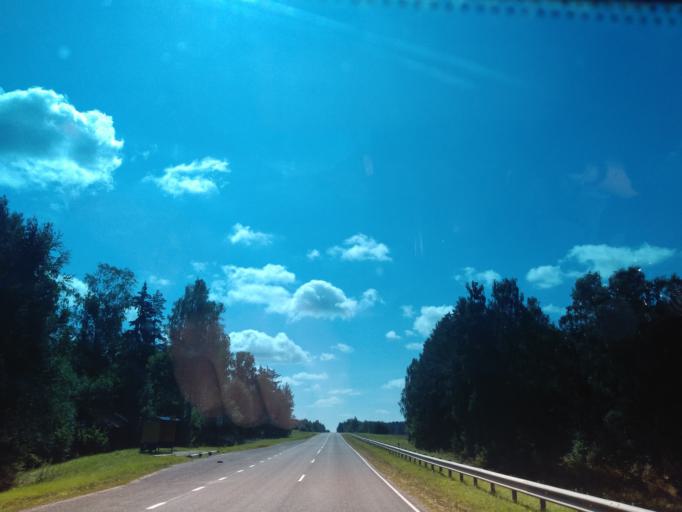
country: BY
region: Minsk
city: Uzda
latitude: 53.3392
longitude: 27.2288
